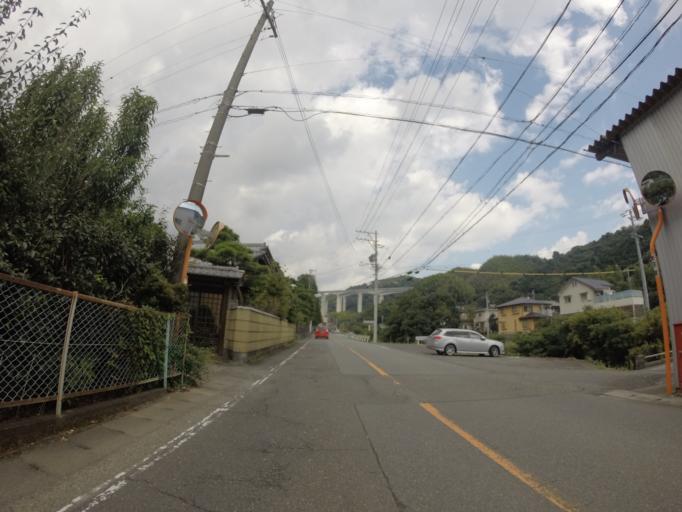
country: JP
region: Shizuoka
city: Shizuoka-shi
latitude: 35.0666
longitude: 138.4693
